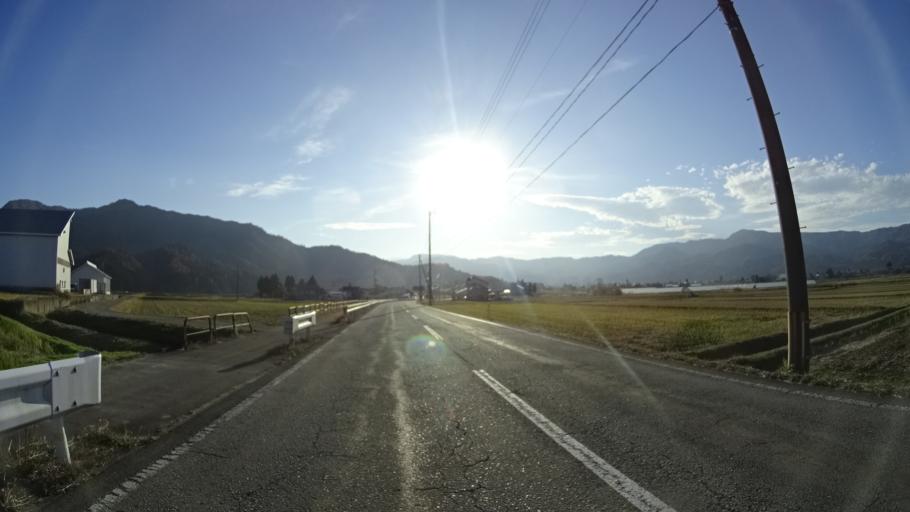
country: JP
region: Niigata
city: Shiozawa
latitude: 37.0130
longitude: 138.8542
